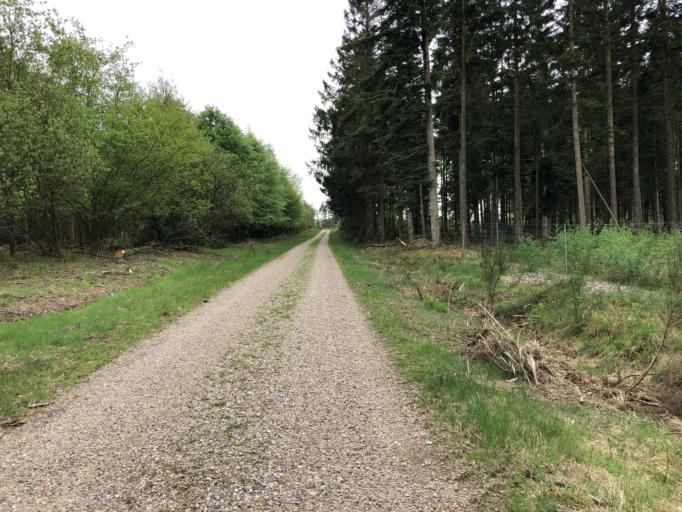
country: DK
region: Central Jutland
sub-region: Holstebro Kommune
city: Ulfborg
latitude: 56.2839
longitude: 8.4337
